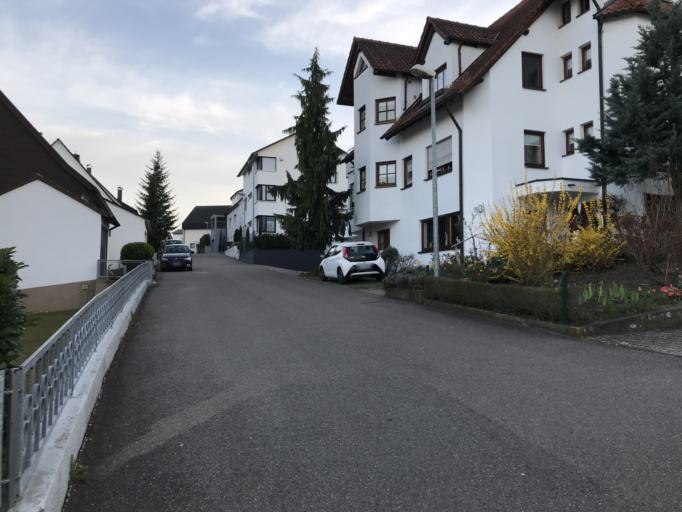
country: DE
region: Baden-Wuerttemberg
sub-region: Regierungsbezirk Stuttgart
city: Unterensingen
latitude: 48.6589
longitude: 9.3529
